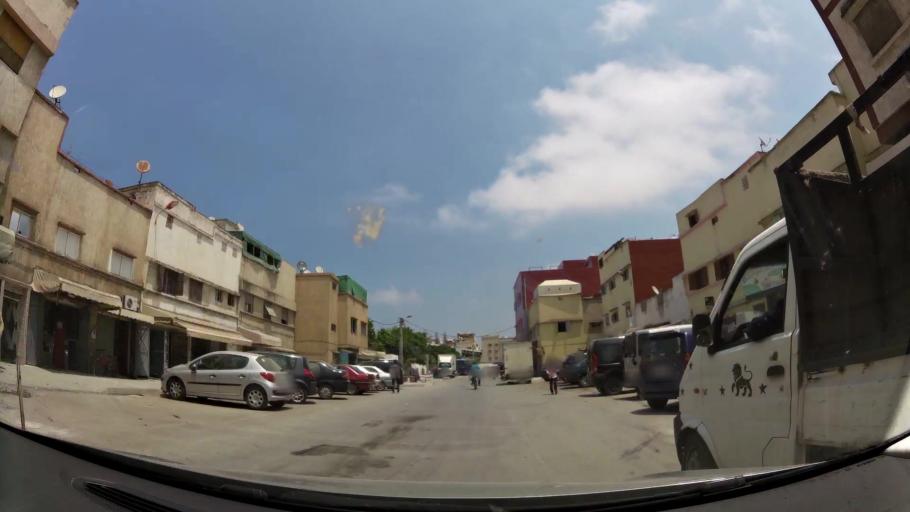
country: MA
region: Rabat-Sale-Zemmour-Zaer
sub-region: Rabat
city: Rabat
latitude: 33.9829
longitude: -6.8827
